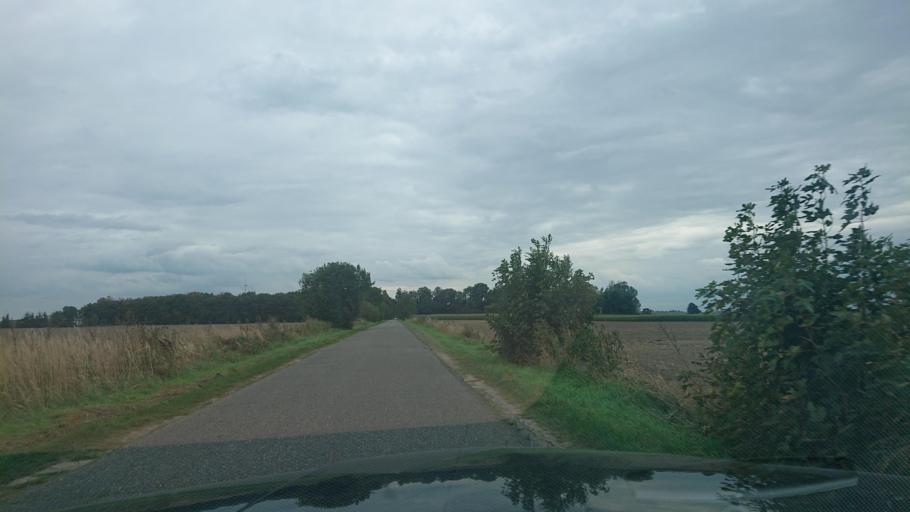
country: PL
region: Greater Poland Voivodeship
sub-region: Powiat gnieznienski
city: Niechanowo
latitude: 52.4608
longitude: 17.6202
